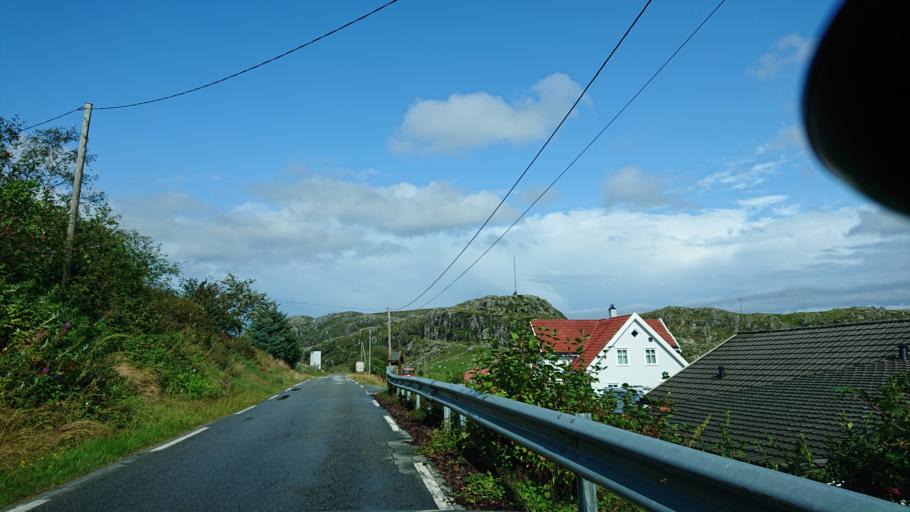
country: NO
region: Rogaland
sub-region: Gjesdal
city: Algard
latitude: 58.6967
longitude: 5.8872
